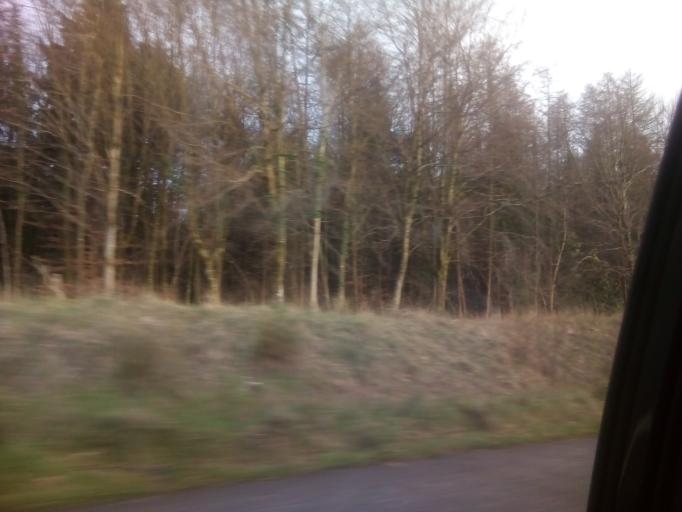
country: IE
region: Leinster
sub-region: Laois
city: Abbeyleix
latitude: 52.9020
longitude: -7.3564
